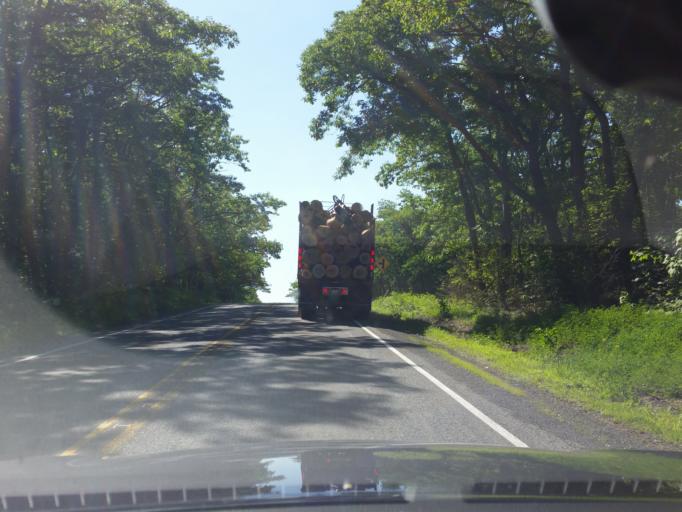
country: US
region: Pennsylvania
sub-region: Lycoming County
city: Duboistown
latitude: 41.1381
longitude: -77.0844
